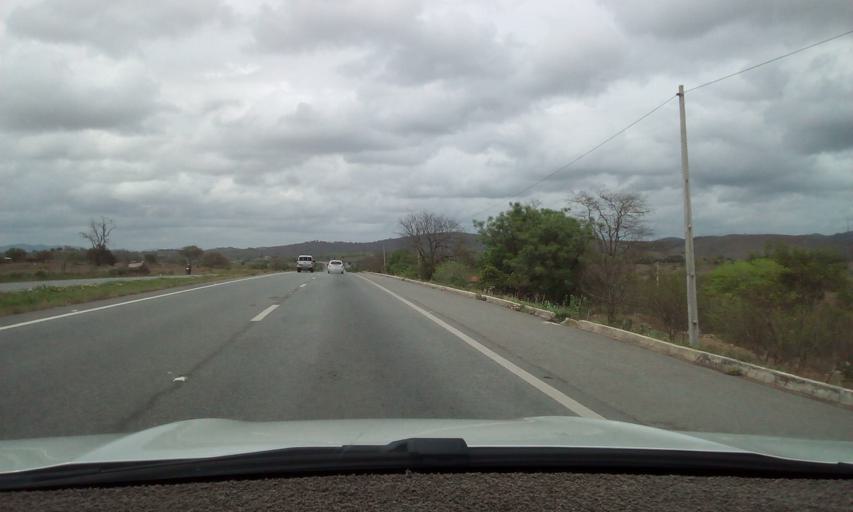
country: BR
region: Paraiba
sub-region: Serra Redonda
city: Alagoa Grande
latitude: -7.2106
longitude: -35.5791
